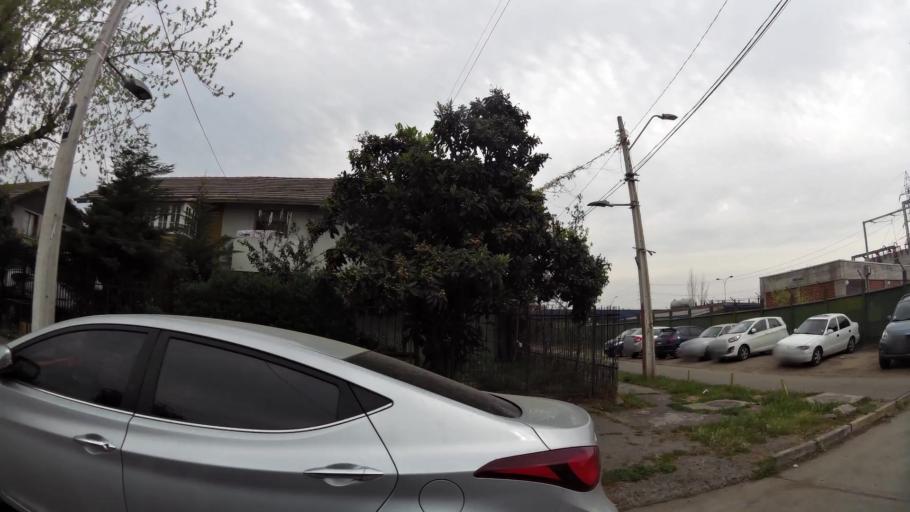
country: CL
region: Santiago Metropolitan
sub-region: Provincia de Santiago
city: Villa Presidente Frei, Nunoa, Santiago, Chile
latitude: -33.4745
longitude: -70.6089
